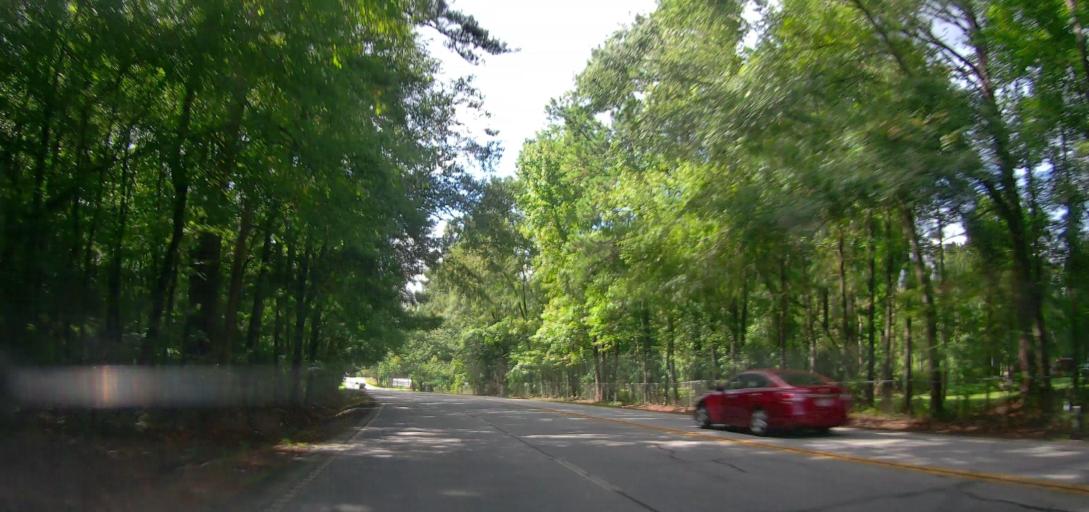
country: US
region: Georgia
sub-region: Harris County
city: Hamilton
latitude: 32.7026
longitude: -84.8602
